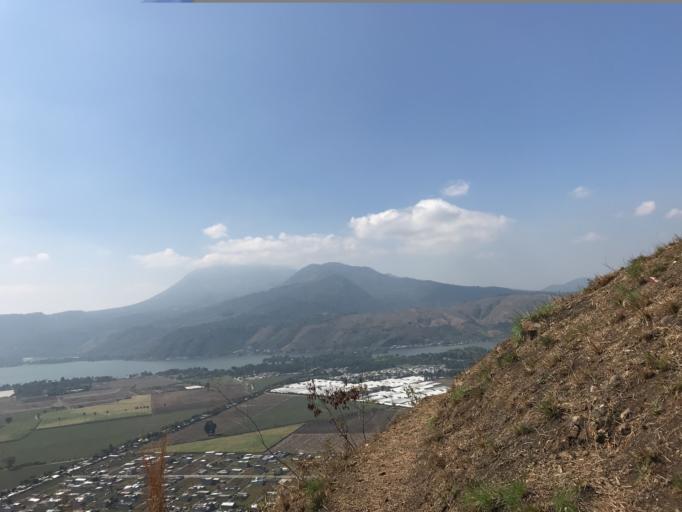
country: GT
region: Guatemala
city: Villa Canales
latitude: 14.4760
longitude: -90.5468
